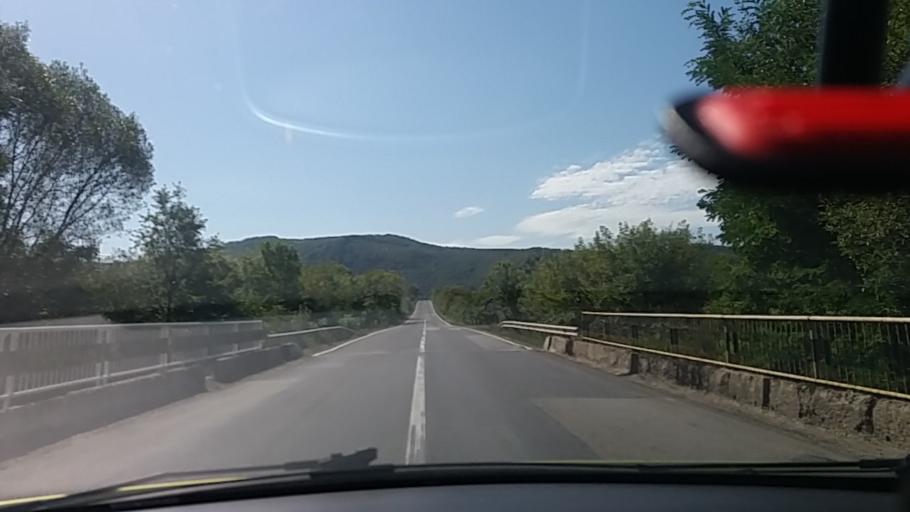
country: RO
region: Hunedoara
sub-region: Comuna Zam
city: Zam
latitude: 45.9882
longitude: 22.4350
